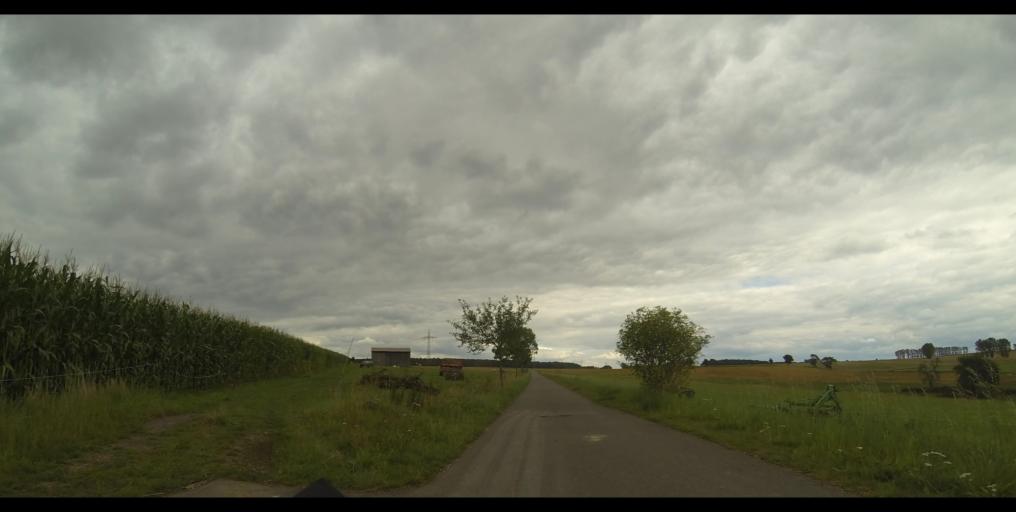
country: DE
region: Saxony
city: Wilsdruff
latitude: 51.0322
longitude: 13.4806
